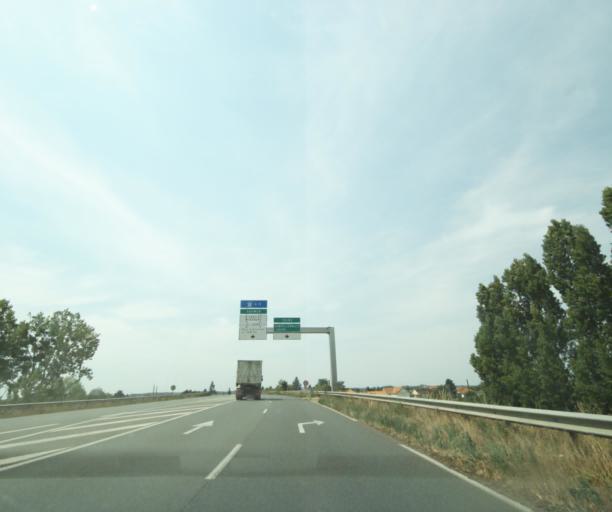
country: FR
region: Poitou-Charentes
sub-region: Departement de la Vienne
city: Antran
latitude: 46.8373
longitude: 0.5516
